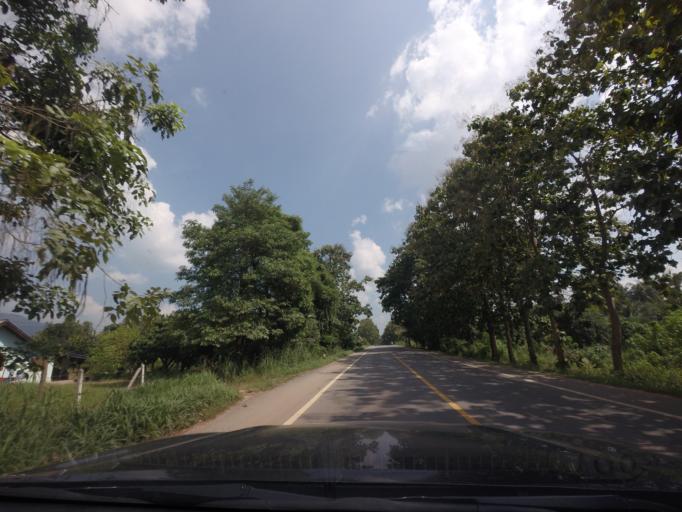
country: TH
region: Phitsanulok
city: Chat Trakan
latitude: 17.2908
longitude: 100.5150
